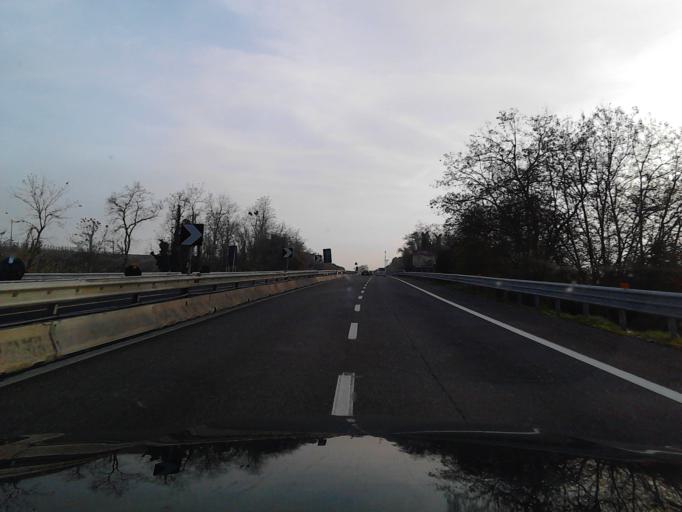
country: IT
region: Abruzzo
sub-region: Provincia di Chieti
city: Marina di San Vito
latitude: 42.3082
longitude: 14.4219
